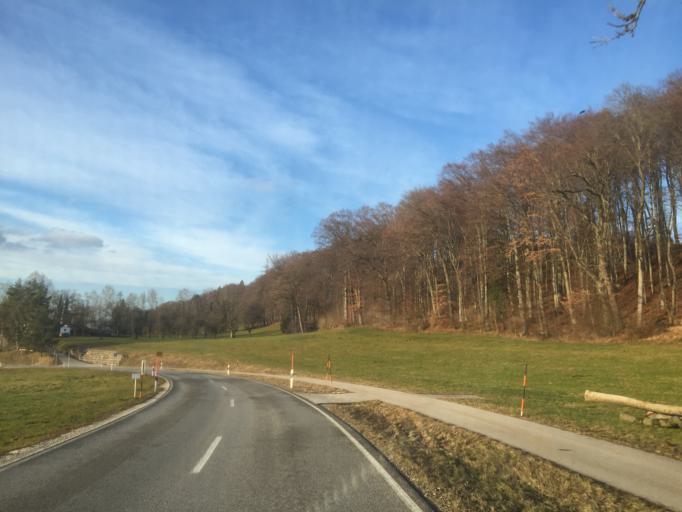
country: DE
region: Bavaria
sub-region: Upper Bavaria
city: Vachendorf
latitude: 47.8490
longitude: 12.6004
